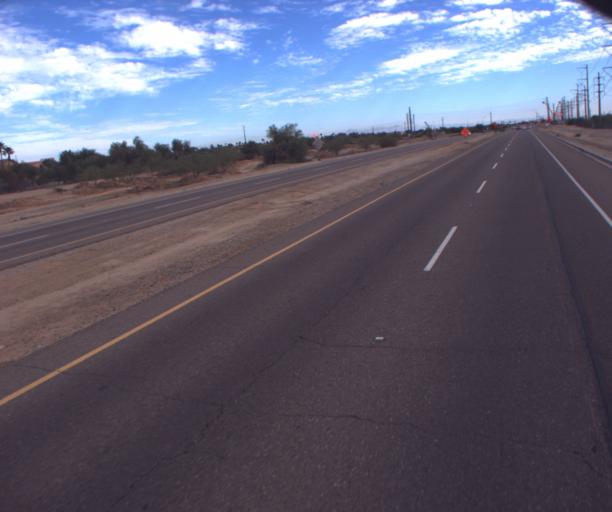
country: US
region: Arizona
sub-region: Maricopa County
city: Guadalupe
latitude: 33.2913
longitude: -112.0038
